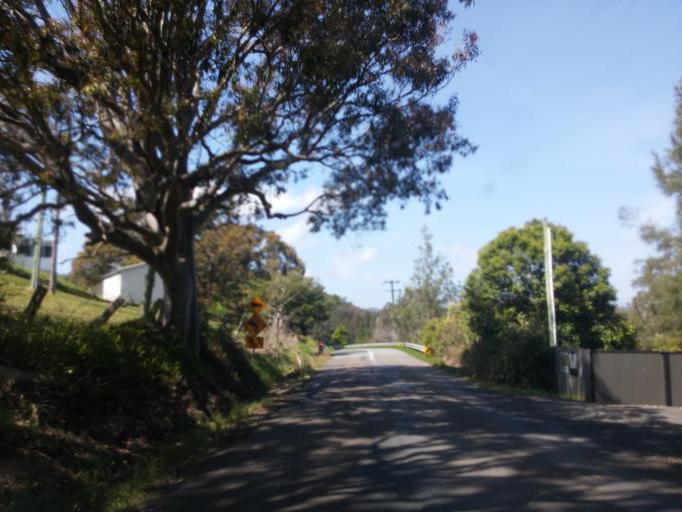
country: AU
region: New South Wales
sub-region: Great Lakes
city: Bulahdelah
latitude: -32.3929
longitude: 152.4372
